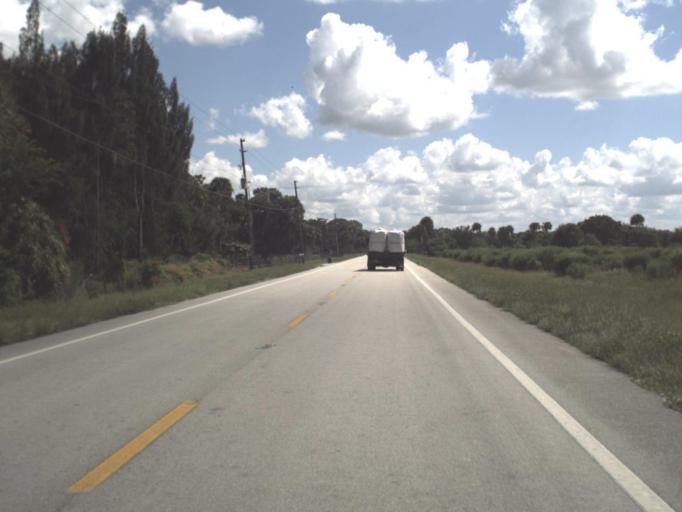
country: US
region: Florida
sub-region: Okeechobee County
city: Taylor Creek
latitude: 27.1539
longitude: -80.7026
